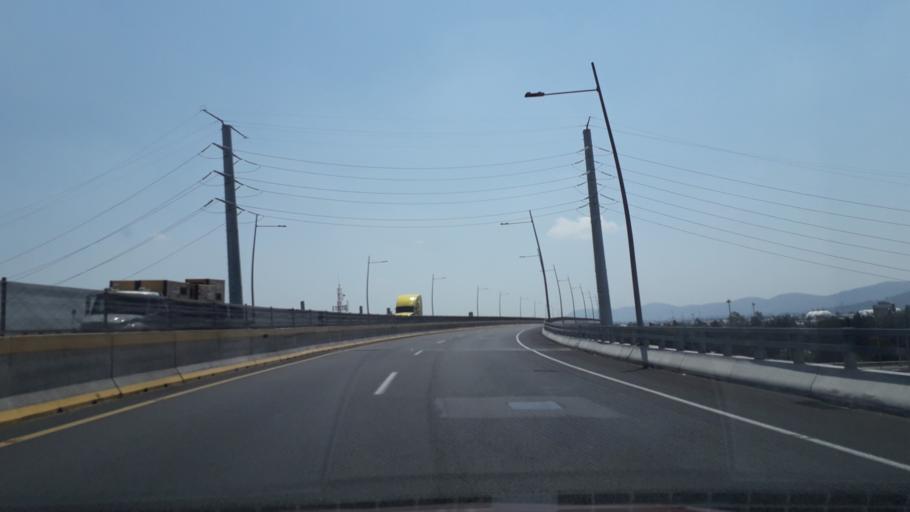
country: MX
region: Puebla
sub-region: Puebla
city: San Sebastian de Aparicio
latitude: 19.0825
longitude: -98.1658
